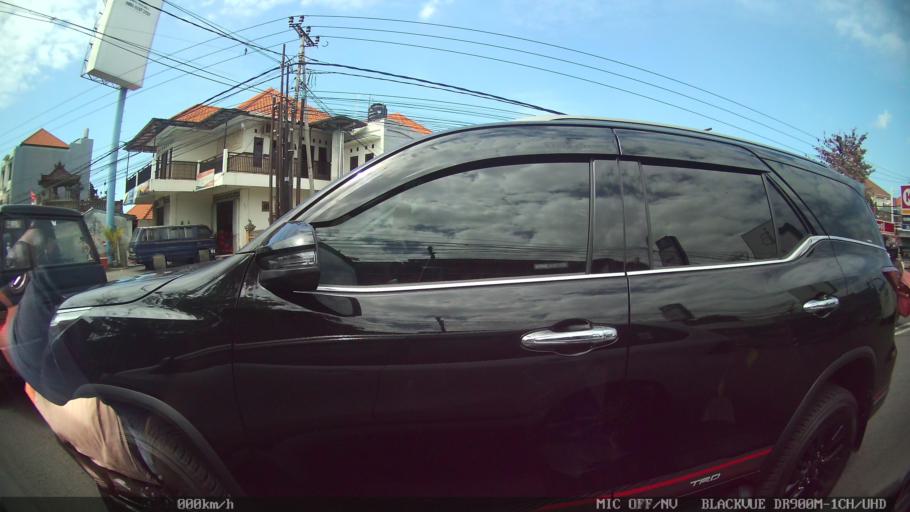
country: ID
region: Bali
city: Karyadharma
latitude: -8.6815
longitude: 115.1951
